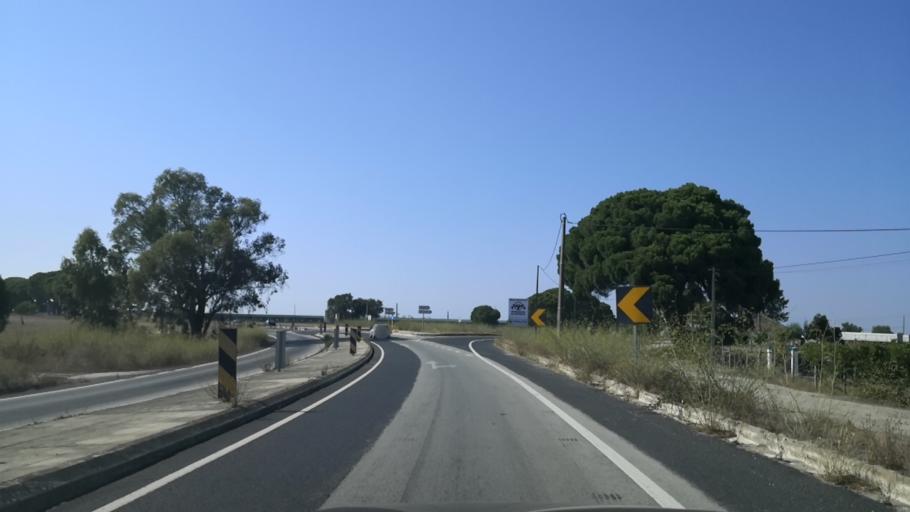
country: PT
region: Evora
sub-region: Vendas Novas
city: Vendas Novas
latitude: 38.7158
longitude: -8.6175
